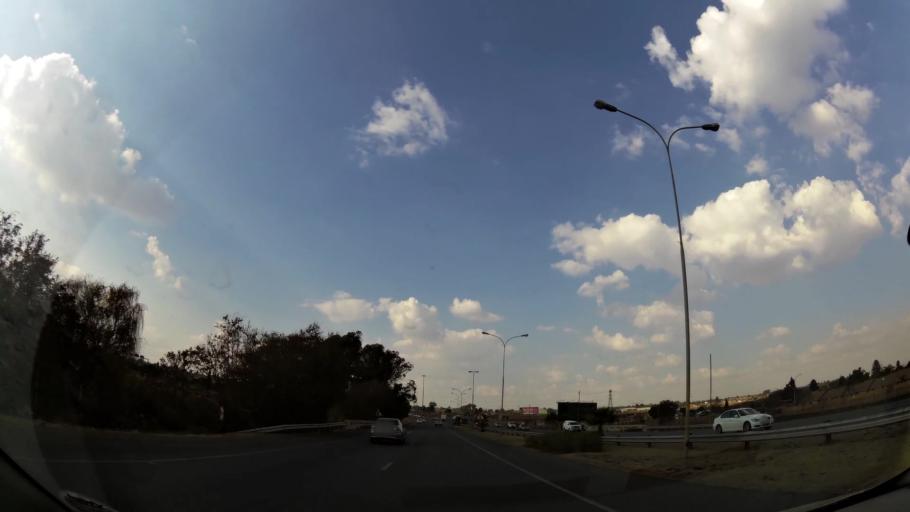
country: ZA
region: Gauteng
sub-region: Ekurhuleni Metropolitan Municipality
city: Brakpan
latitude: -26.2594
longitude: 28.3200
